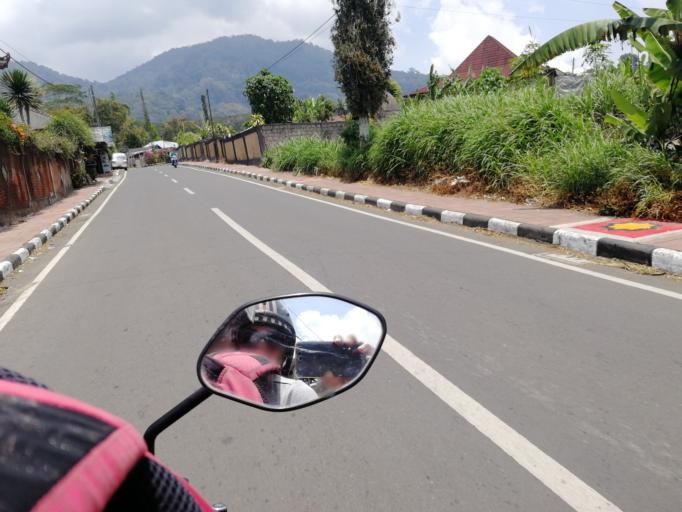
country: ID
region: Bali
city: Munduk
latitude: -8.2841
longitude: 115.1595
